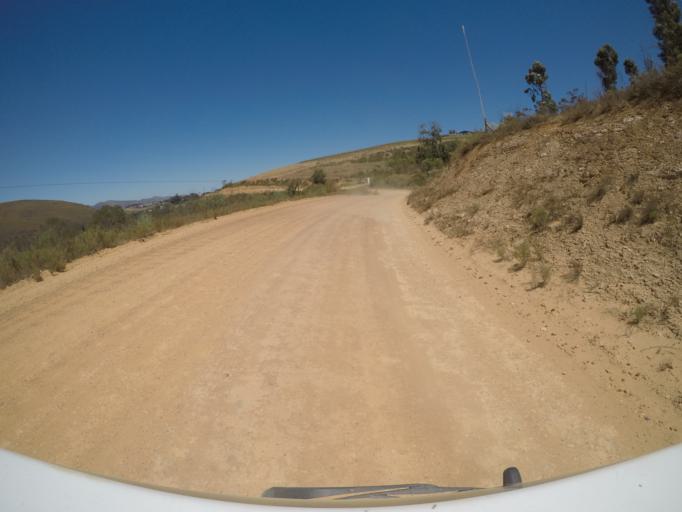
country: ZA
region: Western Cape
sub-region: Overberg District Municipality
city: Grabouw
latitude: -34.2134
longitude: 19.2105
